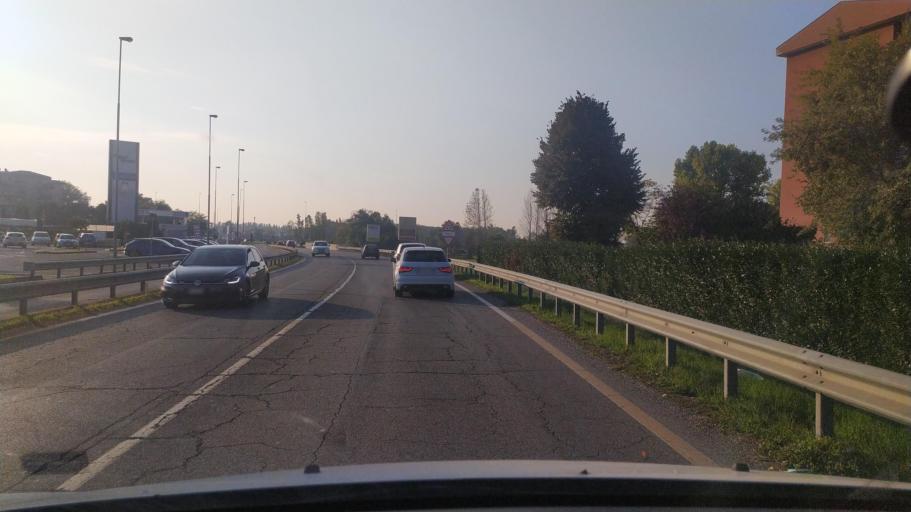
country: IT
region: Lombardy
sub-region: Provincia di Cremona
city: Crema
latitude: 45.3600
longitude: 9.6674
